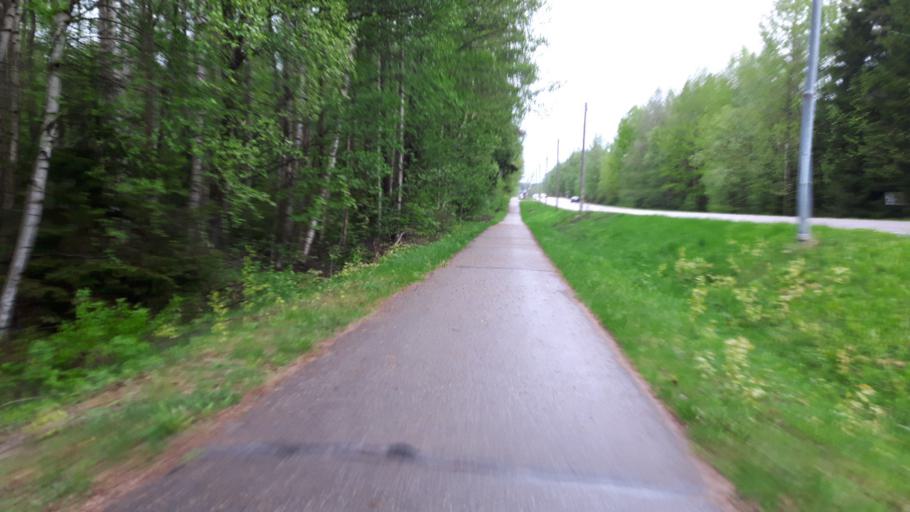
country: FI
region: Kymenlaakso
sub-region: Kotka-Hamina
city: Karhula
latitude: 60.5439
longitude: 26.9756
